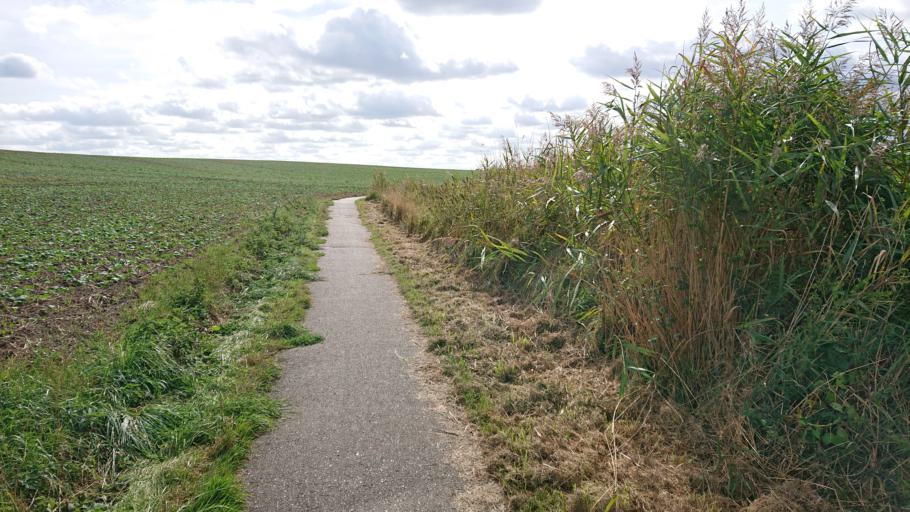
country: DE
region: Mecklenburg-Vorpommern
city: Altefahr
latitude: 54.3458
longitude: 13.1189
